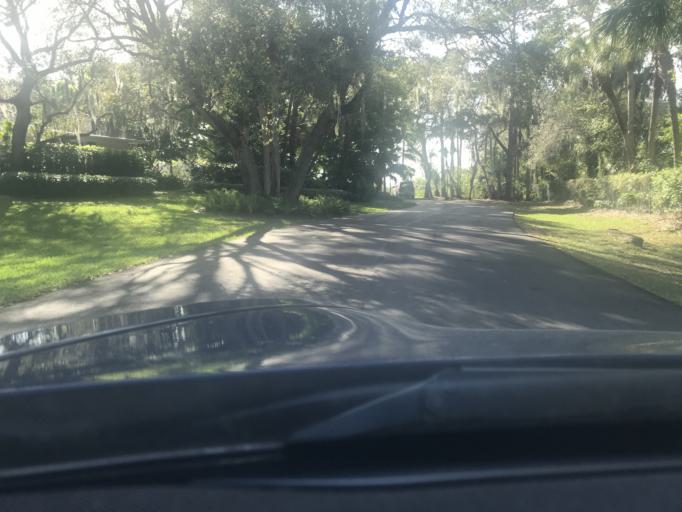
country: US
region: Florida
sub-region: Indian River County
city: Vero Beach South
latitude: 27.6017
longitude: -80.4339
